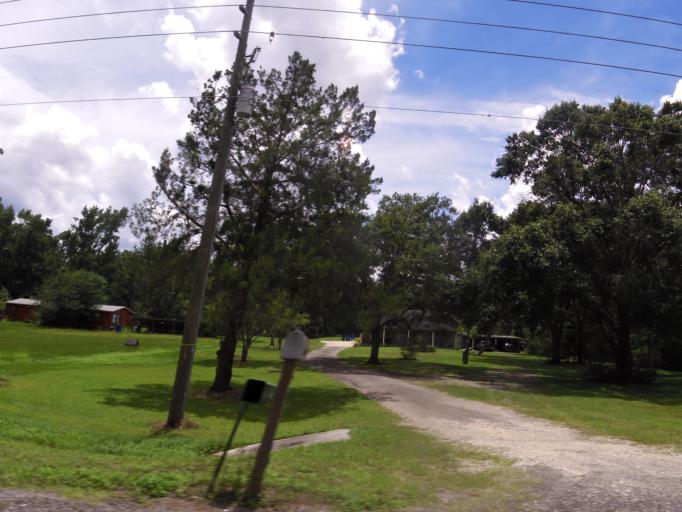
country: US
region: Florida
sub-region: Putnam County
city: East Palatka
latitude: 29.6800
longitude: -81.4691
